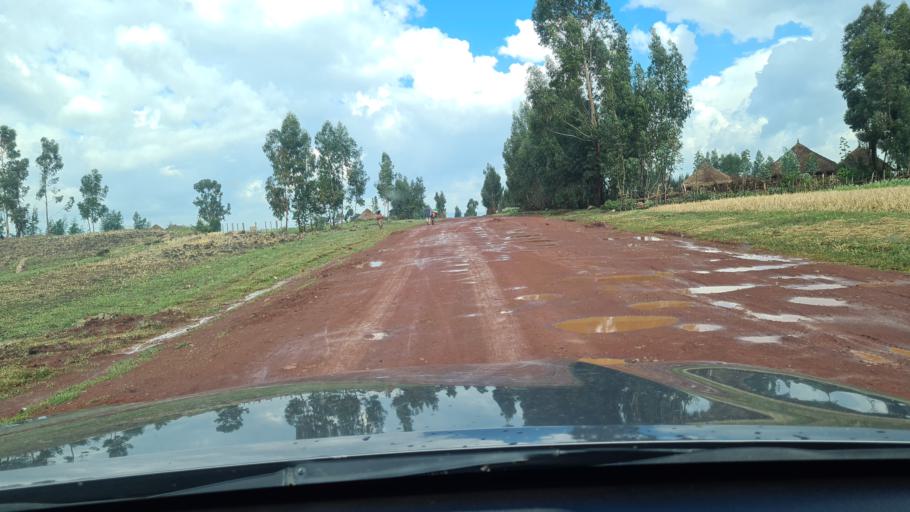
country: ET
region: Oromiya
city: Huruta
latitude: 8.0072
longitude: 39.5697
